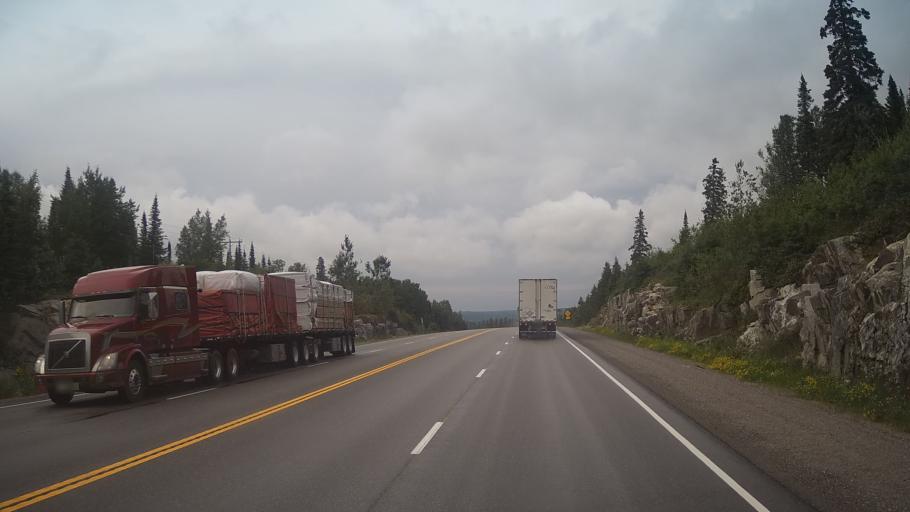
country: CA
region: Ontario
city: Neebing
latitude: 48.6993
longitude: -89.8909
